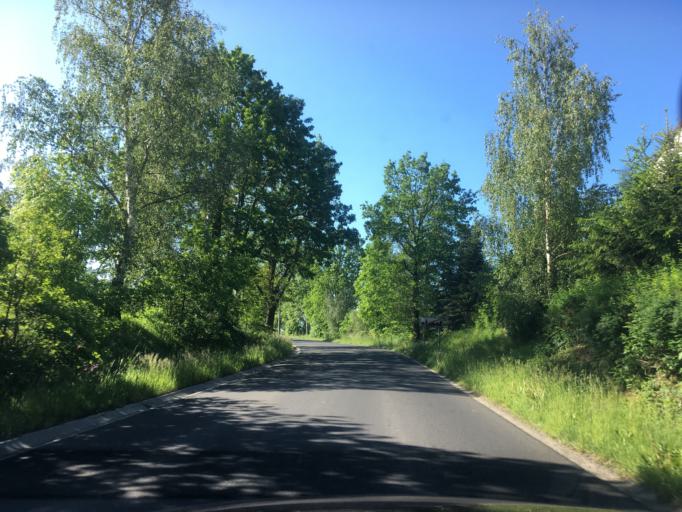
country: PL
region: Lower Silesian Voivodeship
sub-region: Powiat zgorzelecki
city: Zgorzelec
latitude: 51.1100
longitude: 15.0333
